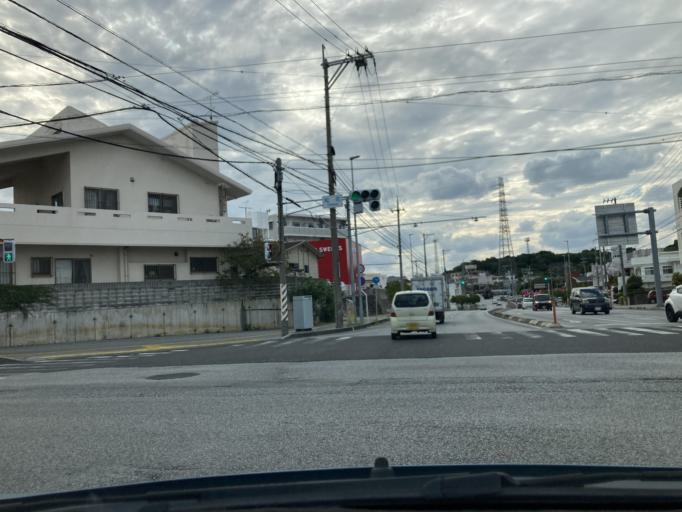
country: JP
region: Okinawa
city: Okinawa
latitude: 26.3607
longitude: 127.8133
